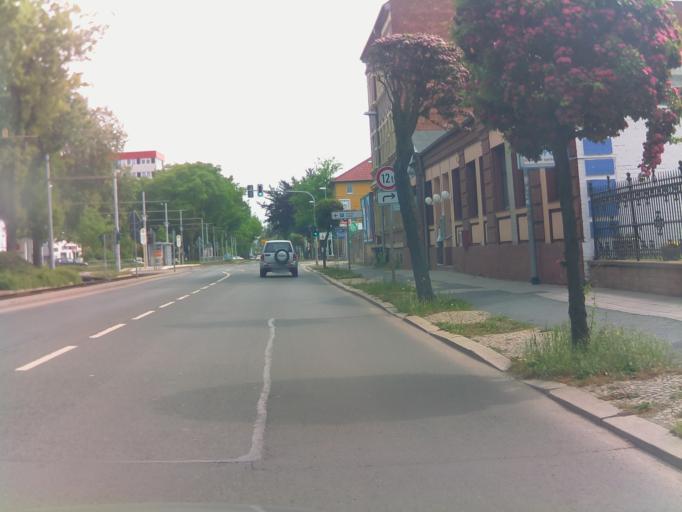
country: DE
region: Thuringia
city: Nordhausen
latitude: 51.5032
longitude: 10.7863
